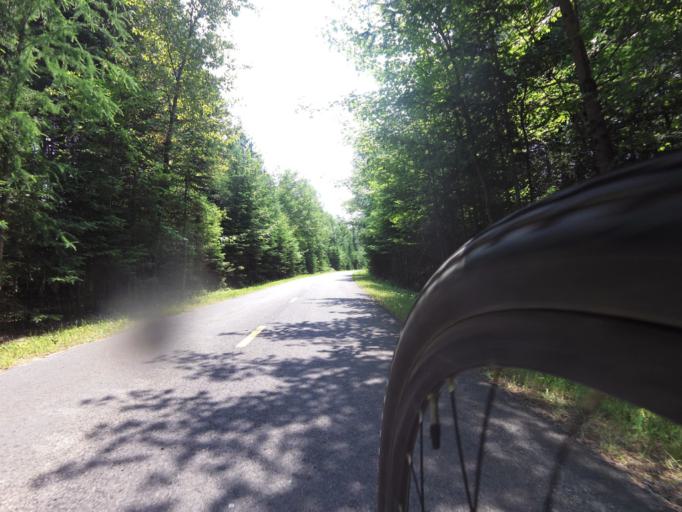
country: CA
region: Quebec
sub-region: Laurentides
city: Mont-Tremblant
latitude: 46.1523
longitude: -74.5943
